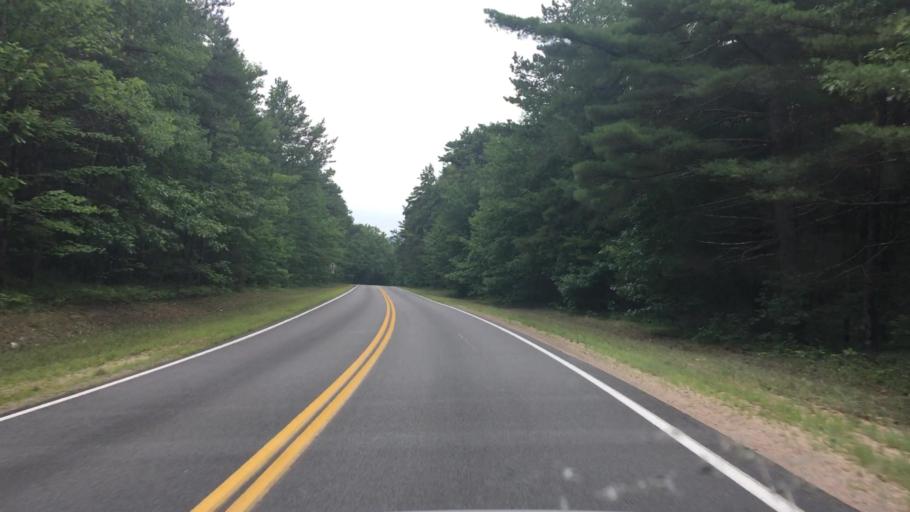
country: US
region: New York
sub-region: Clinton County
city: Morrisonville
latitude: 44.6203
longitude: -73.6191
